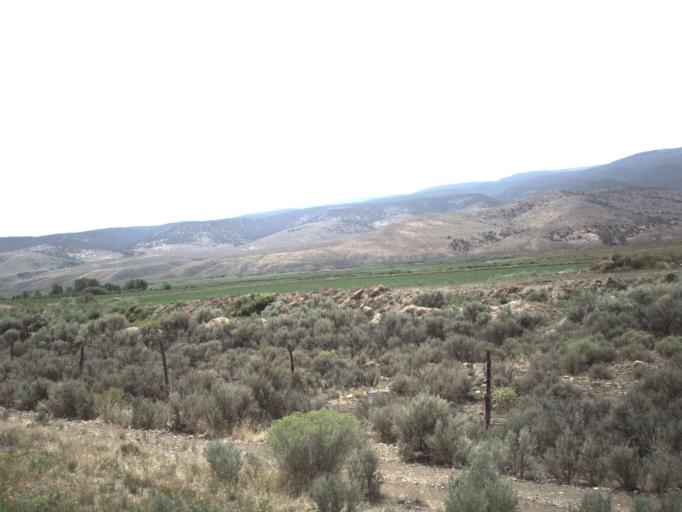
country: US
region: Utah
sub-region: Piute County
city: Junction
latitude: 38.1365
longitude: -111.9978
